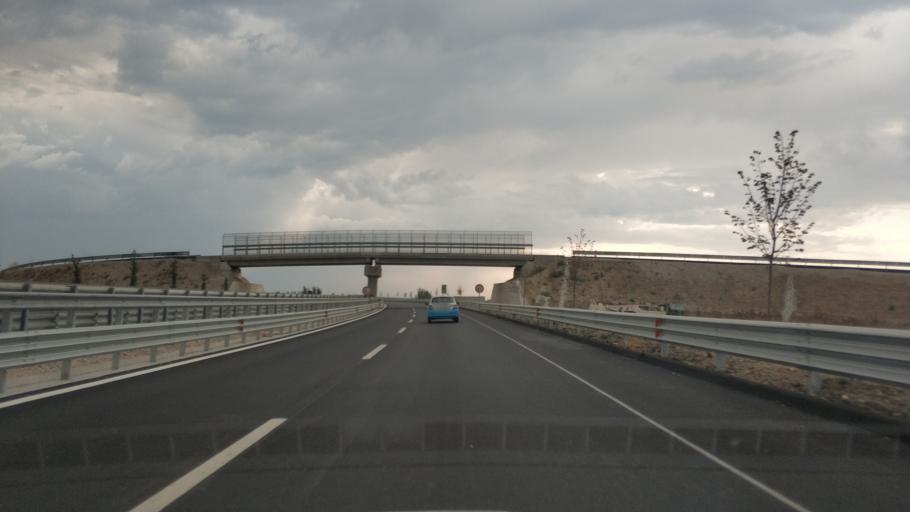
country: AL
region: Fier
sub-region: Rrethi i Fierit
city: Topoje
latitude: 40.7376
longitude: 19.4540
